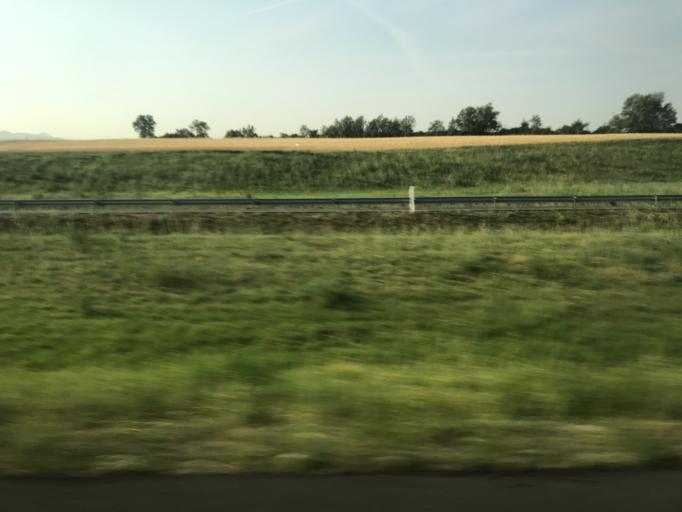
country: ES
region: Basque Country
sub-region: Provincia de Alava
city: Arminon
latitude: 42.7103
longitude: -2.9059
